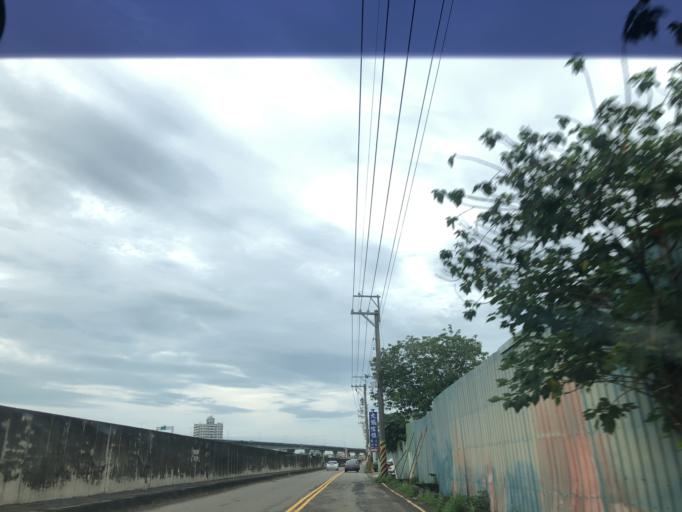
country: TW
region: Taiwan
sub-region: Taichung City
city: Taichung
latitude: 24.1195
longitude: 120.7031
